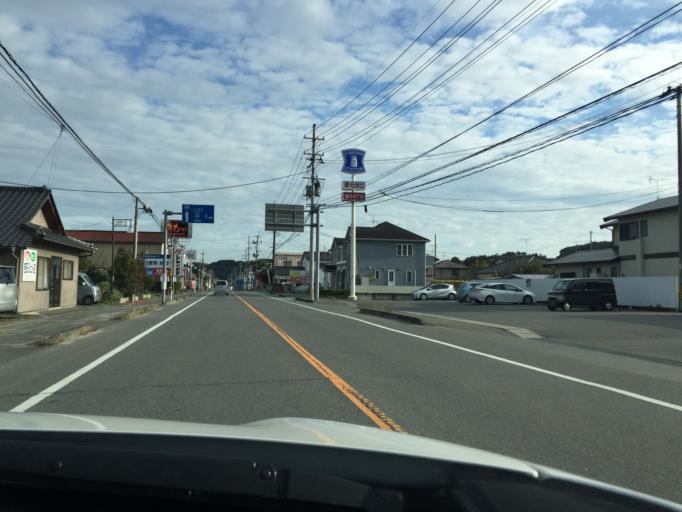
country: JP
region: Fukushima
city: Iwaki
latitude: 37.0650
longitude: 140.8526
